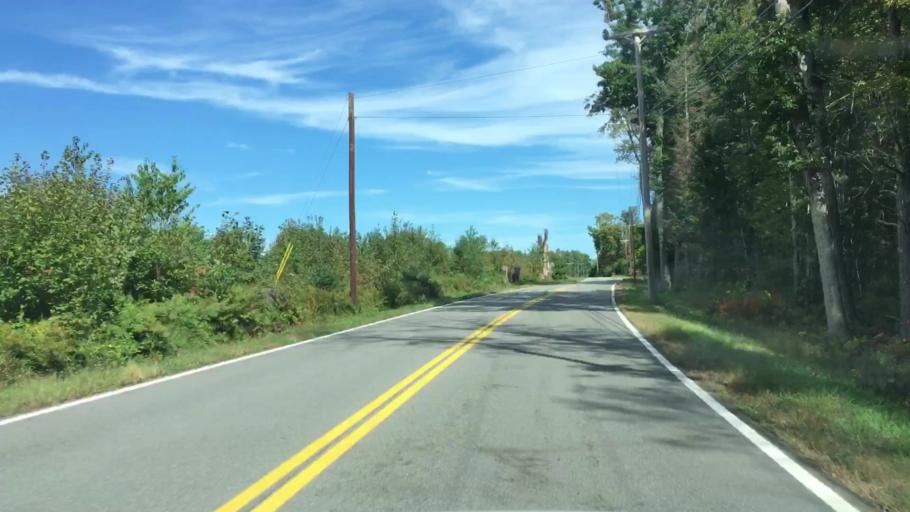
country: US
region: Maine
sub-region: York County
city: Saco
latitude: 43.5617
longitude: -70.4896
